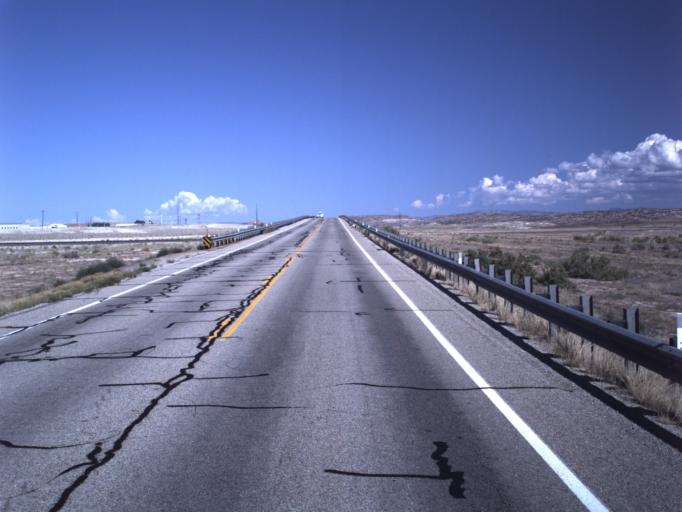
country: US
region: Utah
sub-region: Grand County
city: Moab
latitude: 38.7511
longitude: -109.7390
